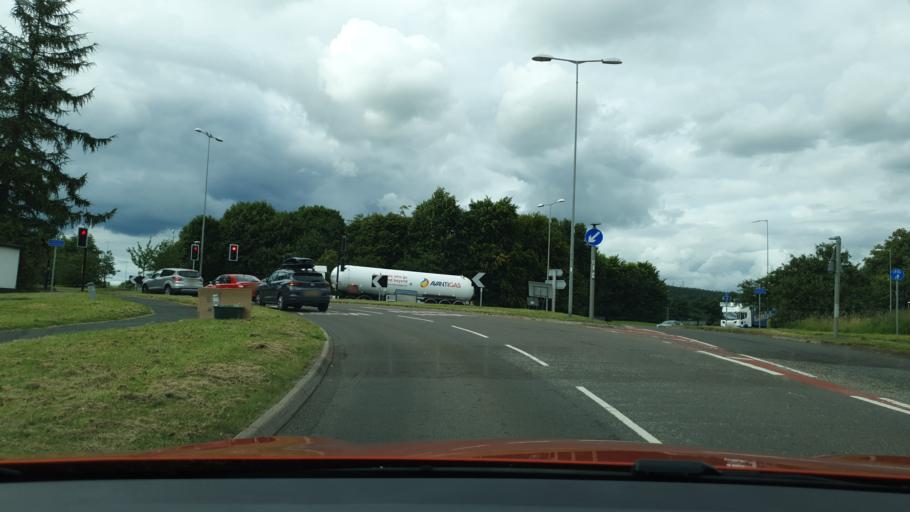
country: GB
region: England
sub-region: Cumbria
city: Penrith
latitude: 54.6536
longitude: -2.7425
